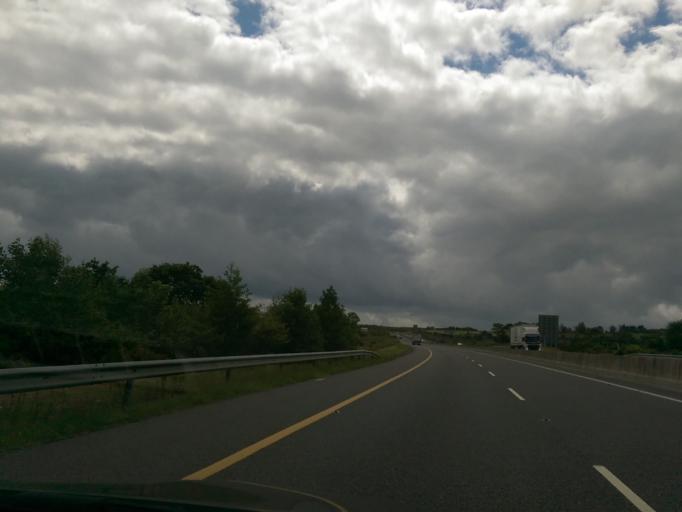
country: IE
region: Munster
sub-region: County Cork
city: Mitchelstown
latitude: 52.2314
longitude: -8.2864
